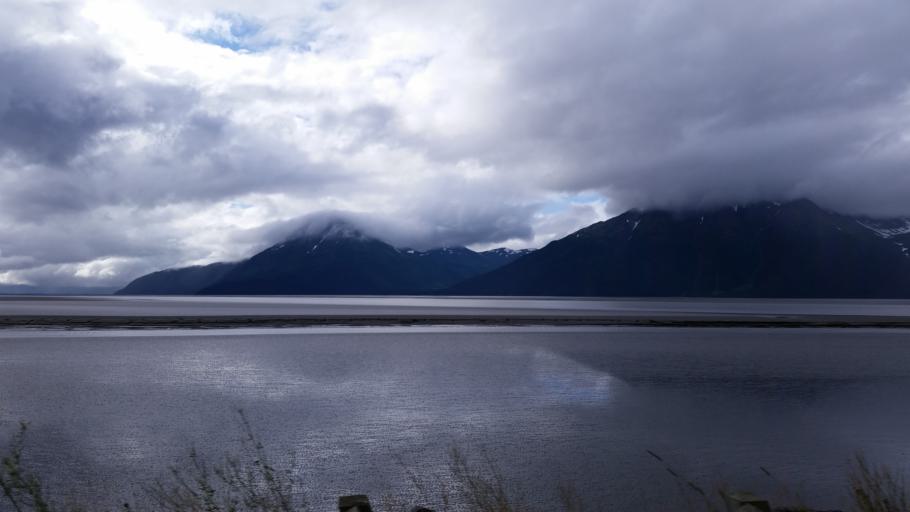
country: US
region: Alaska
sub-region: Anchorage Municipality
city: Girdwood
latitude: 60.9434
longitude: -149.2049
